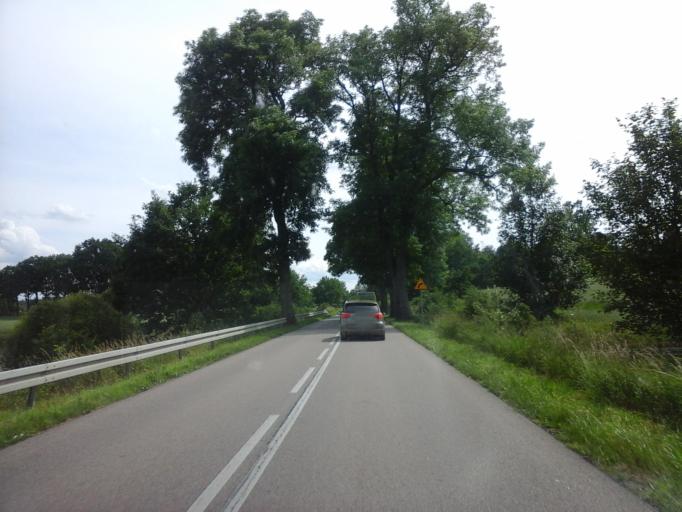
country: PL
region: West Pomeranian Voivodeship
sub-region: Powiat lobeski
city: Wegorzyno
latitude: 53.5726
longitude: 15.5873
